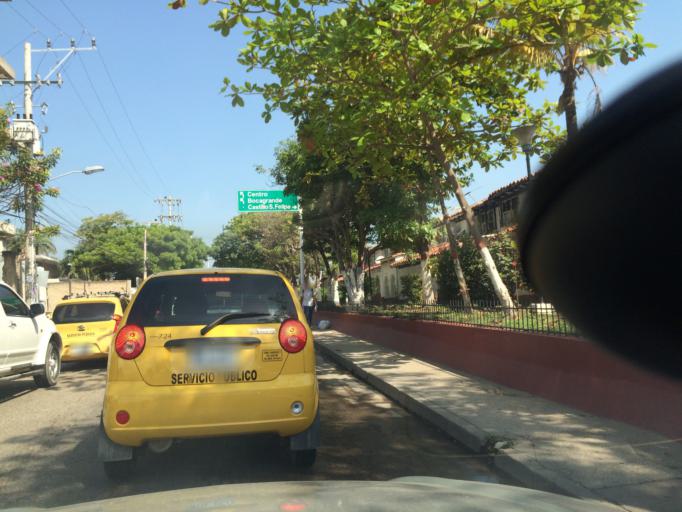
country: CO
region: Bolivar
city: Cartagena
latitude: 10.4179
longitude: -75.5406
